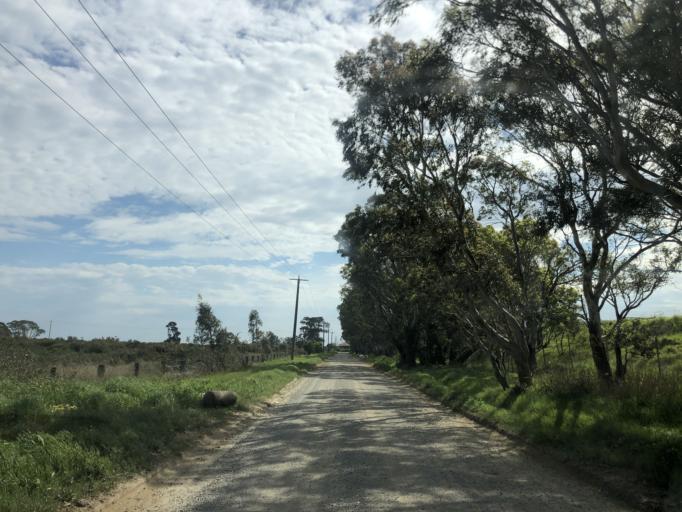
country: AU
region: Victoria
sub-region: Casey
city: Hampton Park
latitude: -38.0466
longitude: 145.2303
